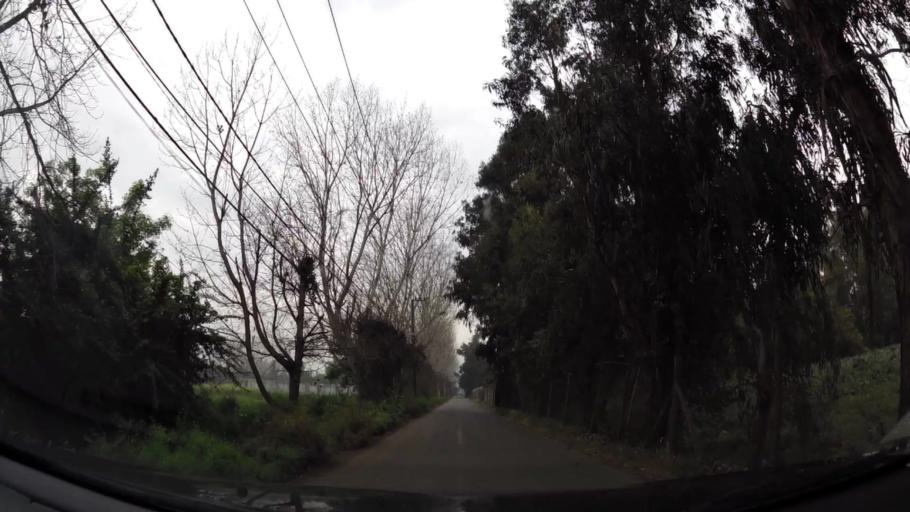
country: CL
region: Santiago Metropolitan
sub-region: Provincia de Chacabuco
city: Lampa
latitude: -33.2429
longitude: -70.7686
